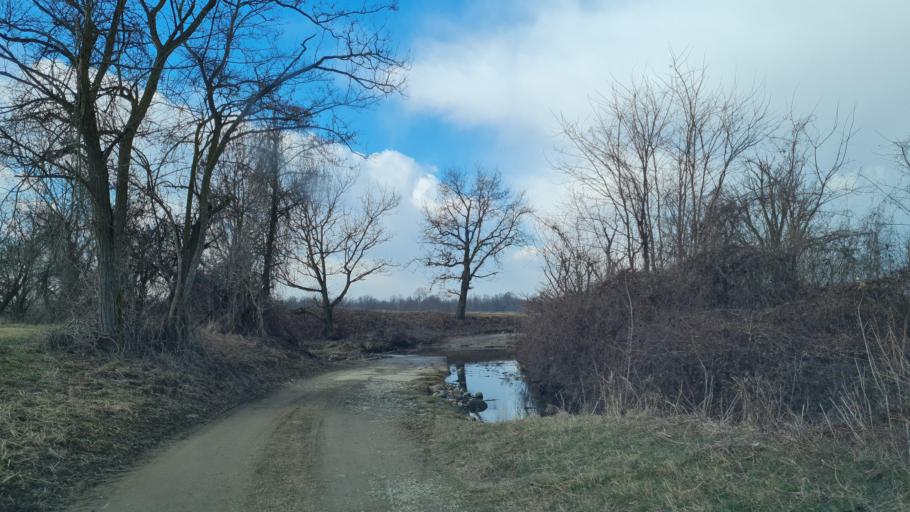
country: IT
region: Piedmont
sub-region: Provincia di Vercelli
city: Buronzo
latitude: 45.4805
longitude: 8.2568
